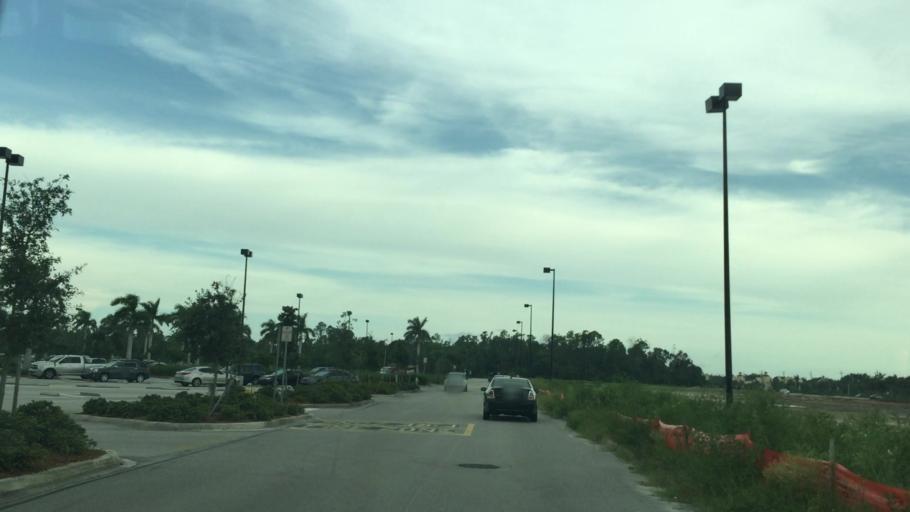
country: US
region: Florida
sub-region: Lee County
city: Fort Myers
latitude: 26.6047
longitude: -81.8100
